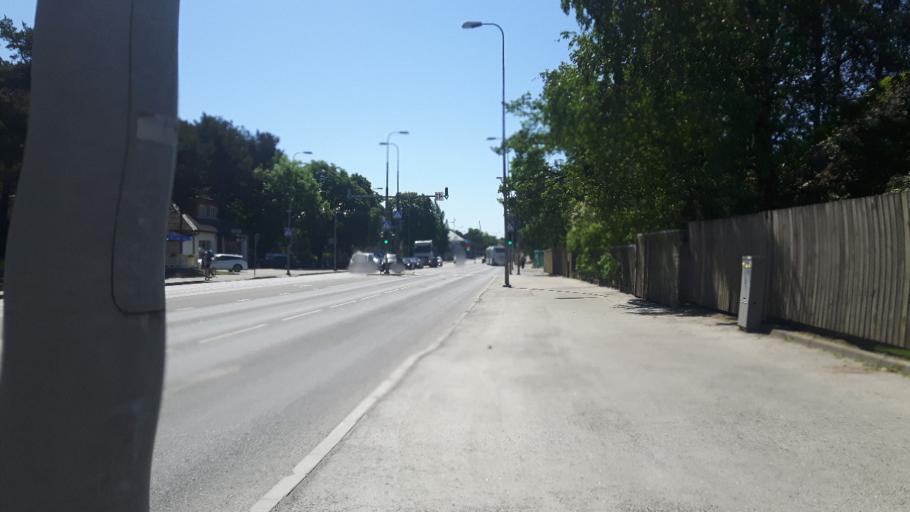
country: EE
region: Harju
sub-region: Tallinna linn
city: Tallinn
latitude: 59.3780
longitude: 24.7176
